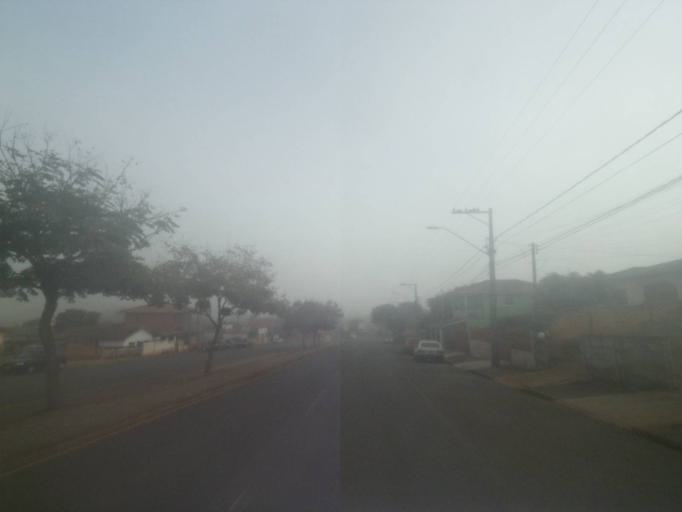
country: BR
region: Parana
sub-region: Tibagi
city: Tibagi
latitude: -24.5115
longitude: -50.4179
